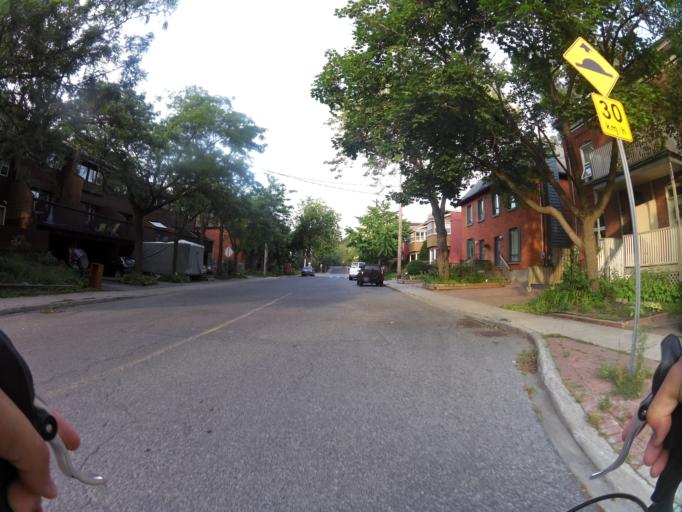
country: CA
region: Ontario
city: Ottawa
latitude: 45.4111
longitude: -75.7132
